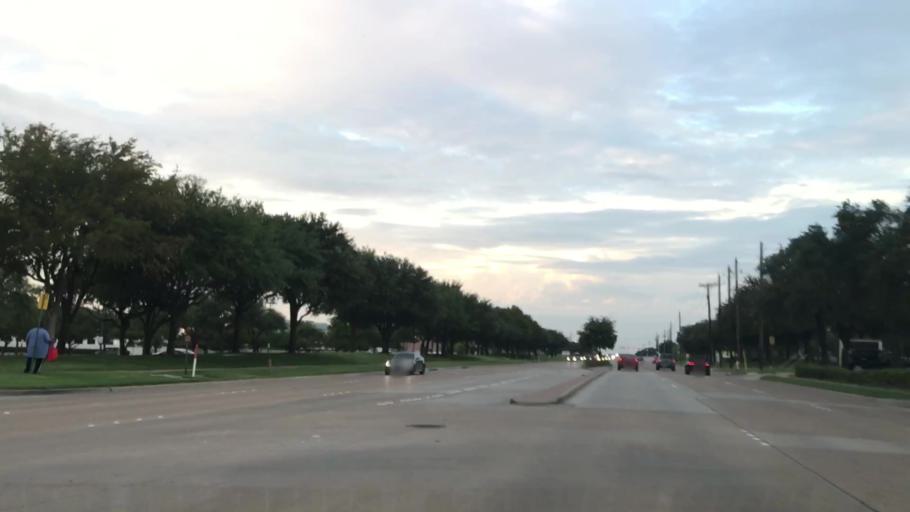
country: US
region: Texas
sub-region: Dallas County
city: Addison
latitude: 33.0208
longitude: -96.8435
